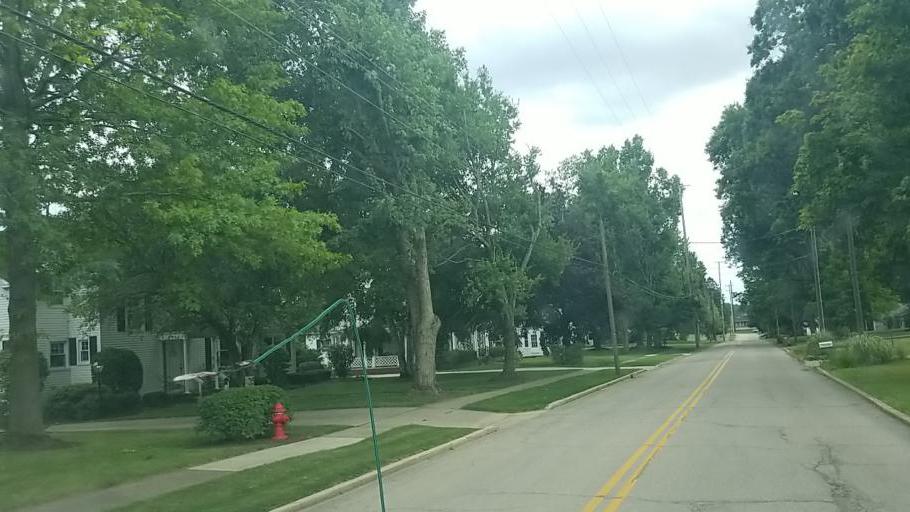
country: US
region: Ohio
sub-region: Medina County
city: Westfield Center
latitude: 41.0236
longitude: -81.9335
